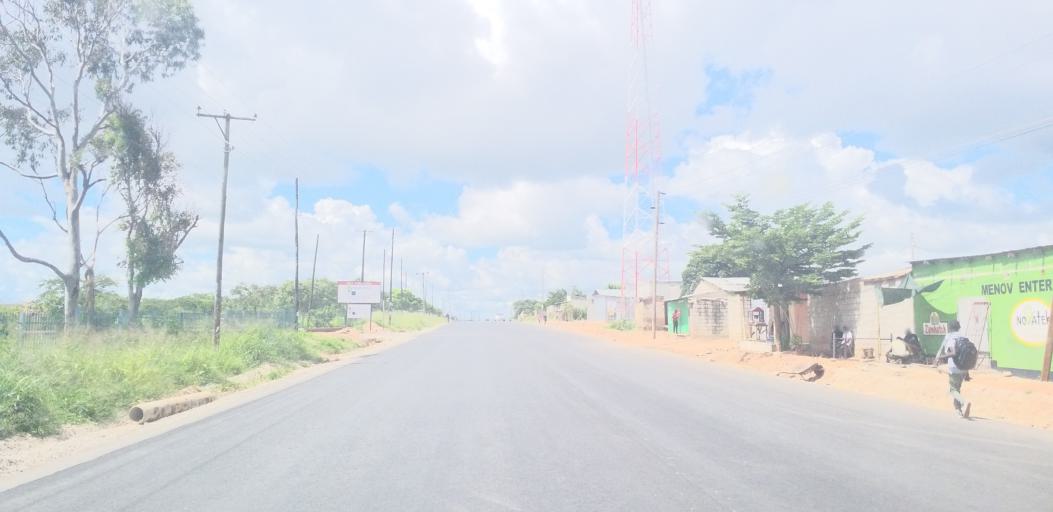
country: ZM
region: Lusaka
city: Lusaka
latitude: -15.3605
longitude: 28.3220
